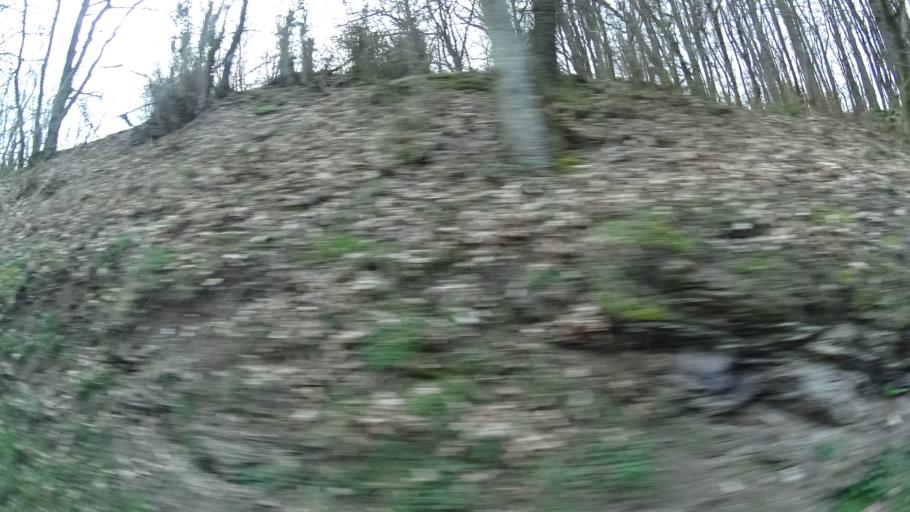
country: DE
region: Rheinland-Pfalz
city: Leisel
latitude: 49.7196
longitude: 7.2090
